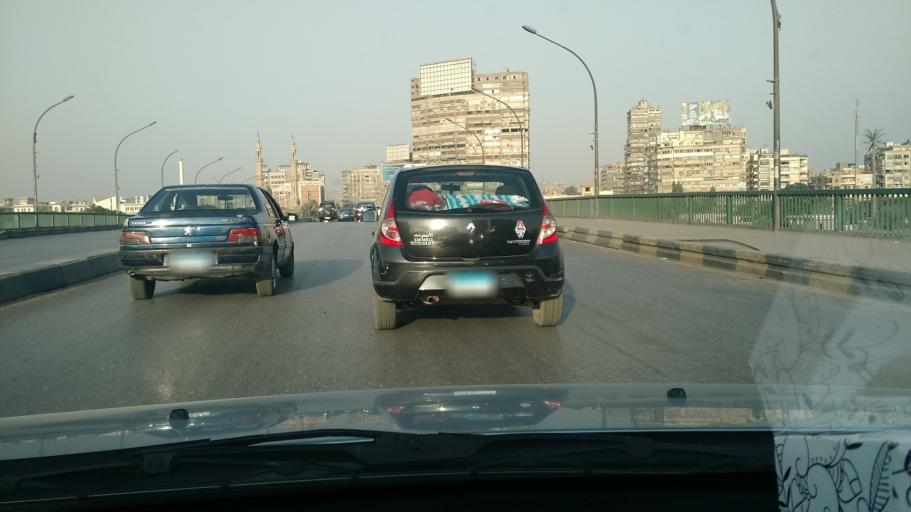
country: EG
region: Al Jizah
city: Al Jizah
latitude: 30.0284
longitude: 31.2201
